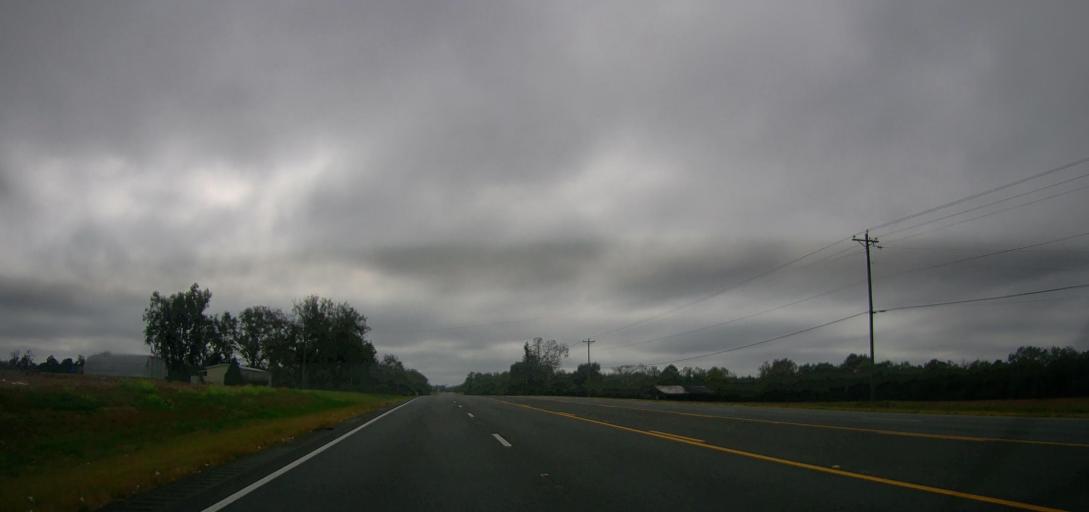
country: US
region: Georgia
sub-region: Thomas County
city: Thomasville
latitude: 30.9647
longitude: -83.8930
